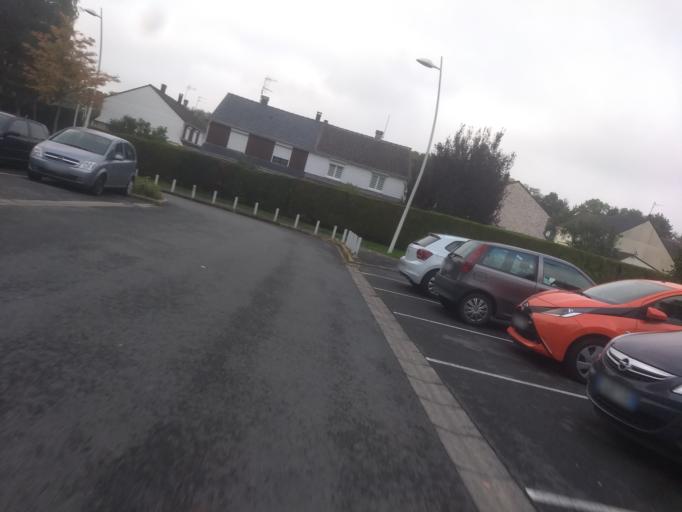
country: FR
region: Nord-Pas-de-Calais
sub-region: Departement du Pas-de-Calais
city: Saint-Nicolas
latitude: 50.3065
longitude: 2.7906
